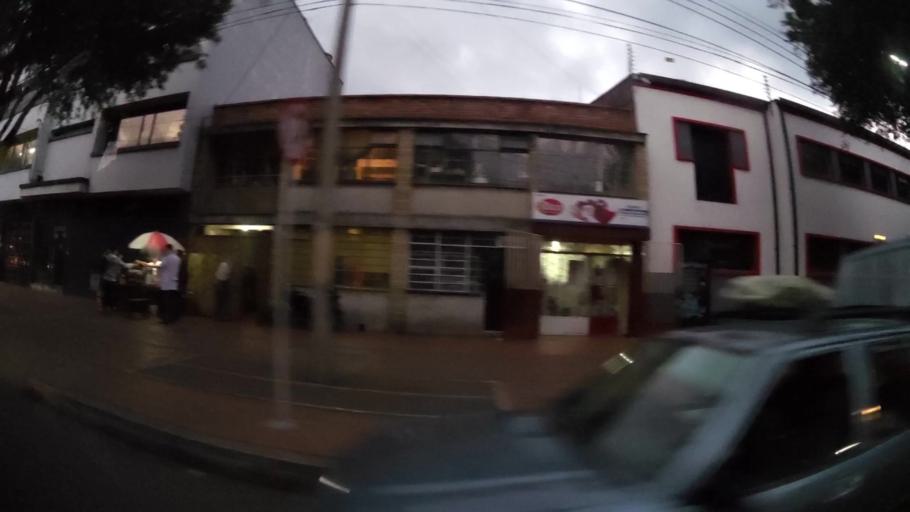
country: CO
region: Bogota D.C.
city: Bogota
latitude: 4.6224
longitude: -74.0809
